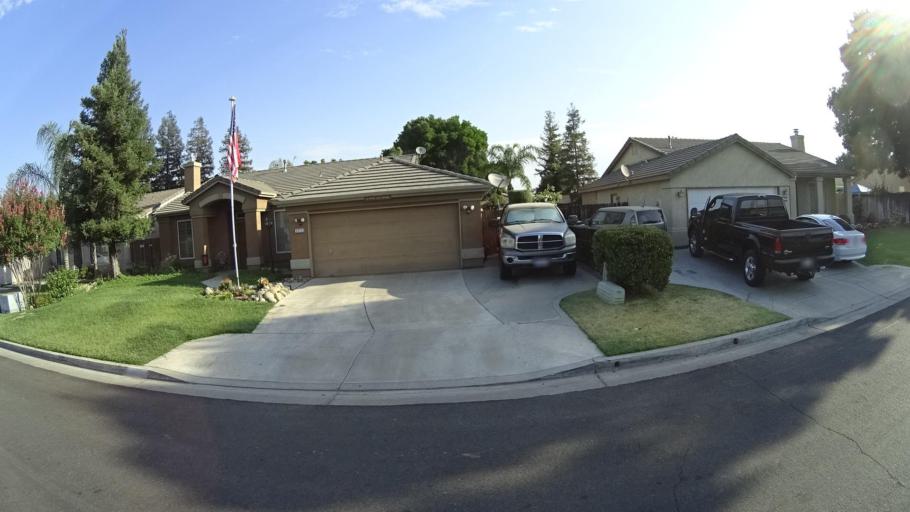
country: US
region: California
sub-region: Fresno County
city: Sunnyside
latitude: 36.7115
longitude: -119.6945
